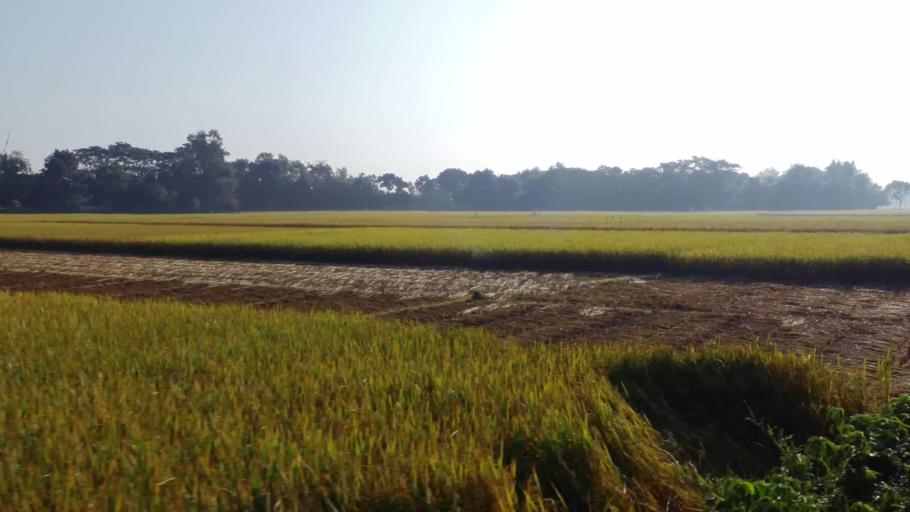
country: BD
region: Dhaka
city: Jamalpur
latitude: 24.8632
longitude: 90.0705
